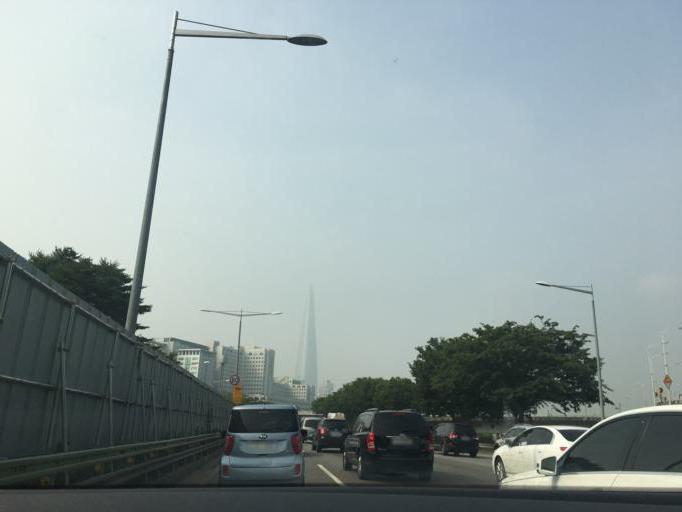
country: KR
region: Gyeonggi-do
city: Guri-si
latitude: 37.5324
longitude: 127.1096
